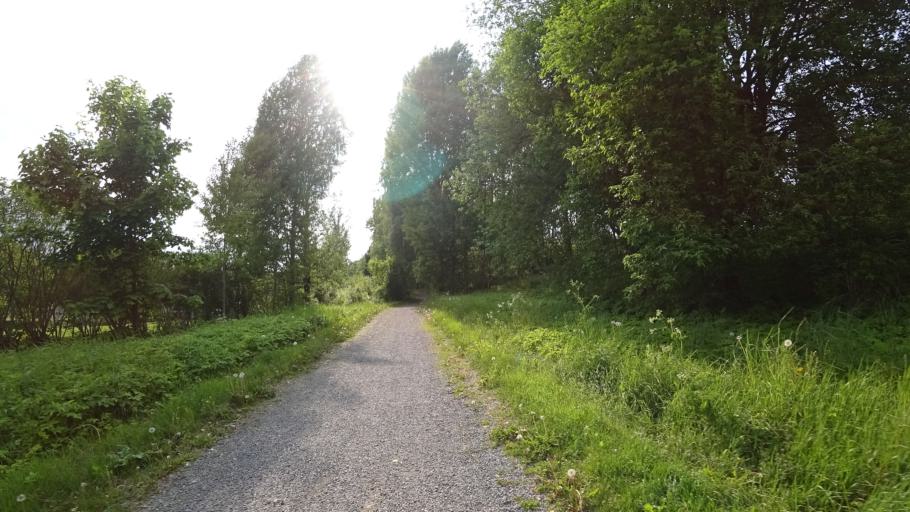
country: FI
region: Pirkanmaa
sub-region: Tampere
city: Pirkkala
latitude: 61.5006
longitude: 23.6618
